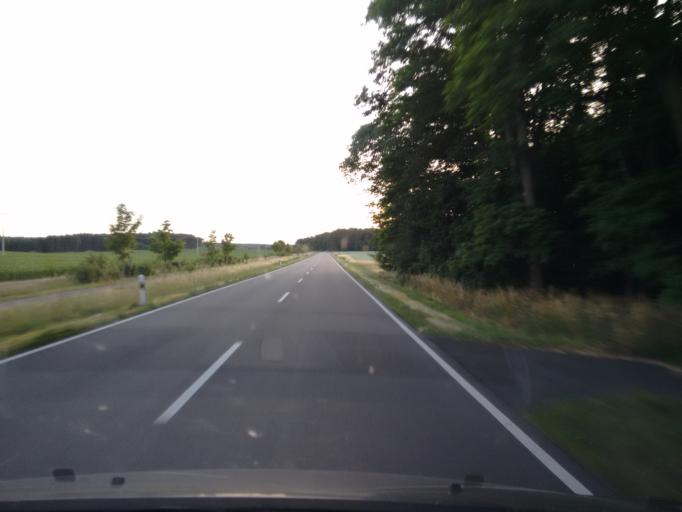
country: DE
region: Brandenburg
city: Gross Lindow
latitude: 52.1428
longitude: 14.5200
